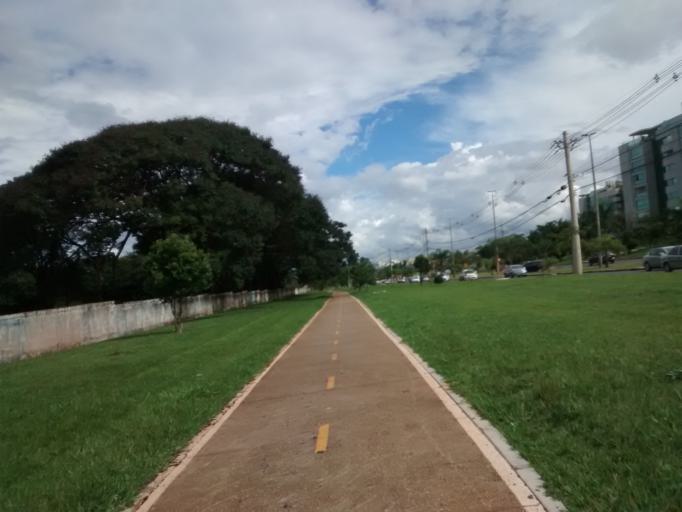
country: BR
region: Federal District
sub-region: Brasilia
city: Brasilia
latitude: -15.7907
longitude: -47.9156
